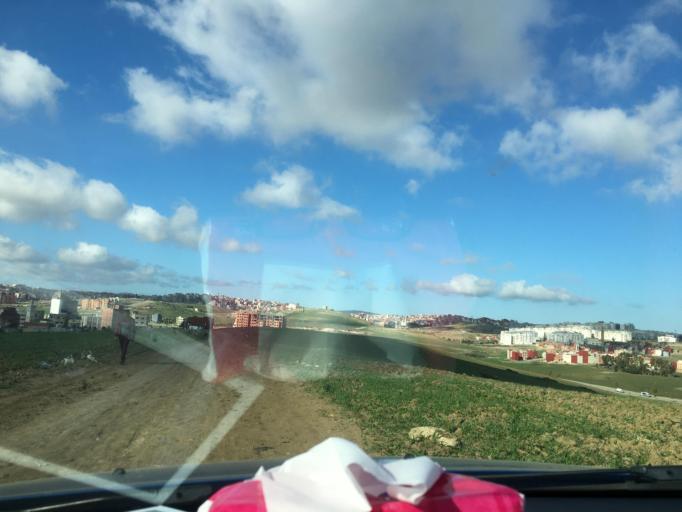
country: MA
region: Tanger-Tetouan
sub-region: Tanger-Assilah
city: Tangier
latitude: 35.7169
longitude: -5.8164
